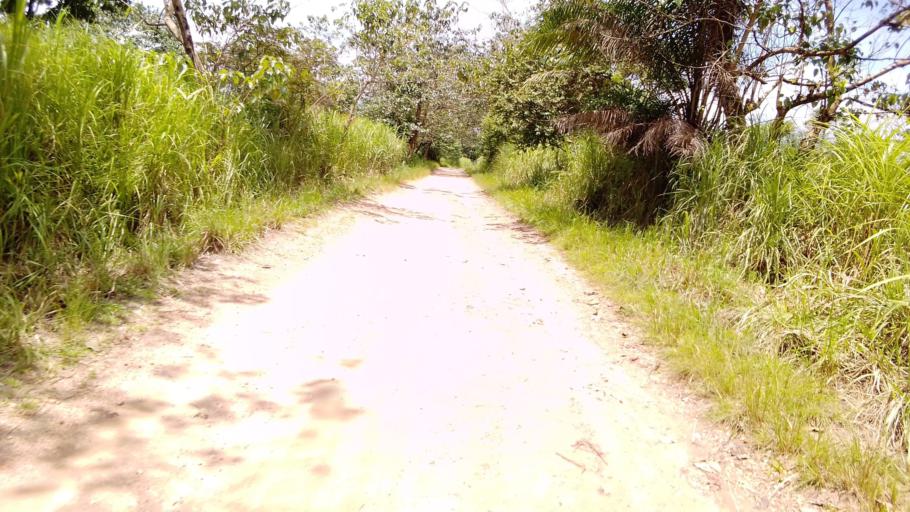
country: SL
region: Eastern Province
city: Koidu
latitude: 8.6939
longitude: -10.9539
